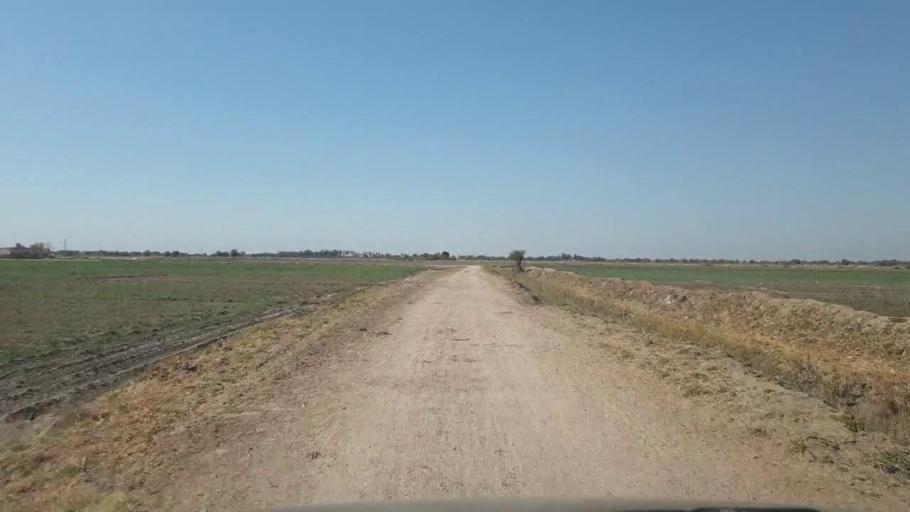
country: PK
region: Sindh
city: Dhoro Naro
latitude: 25.4529
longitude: 69.5982
